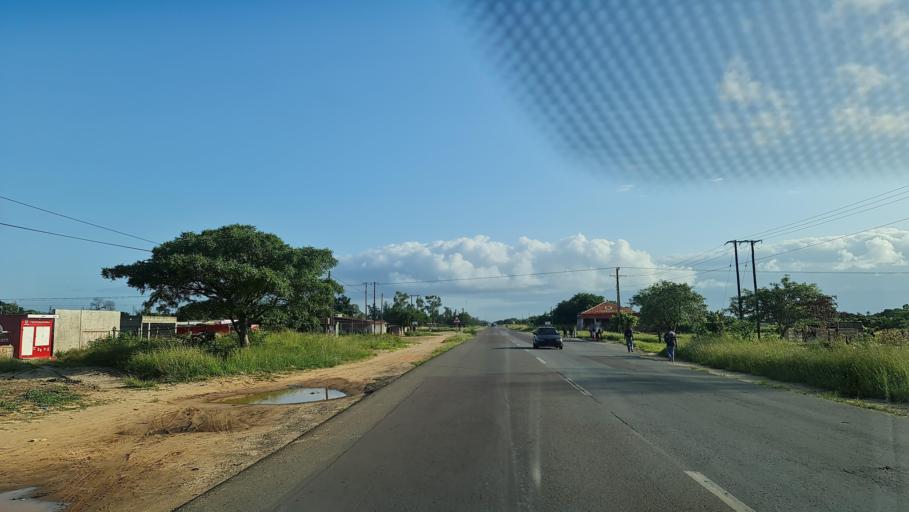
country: MZ
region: Maputo City
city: Maputo
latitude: -25.6838
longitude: 32.6657
